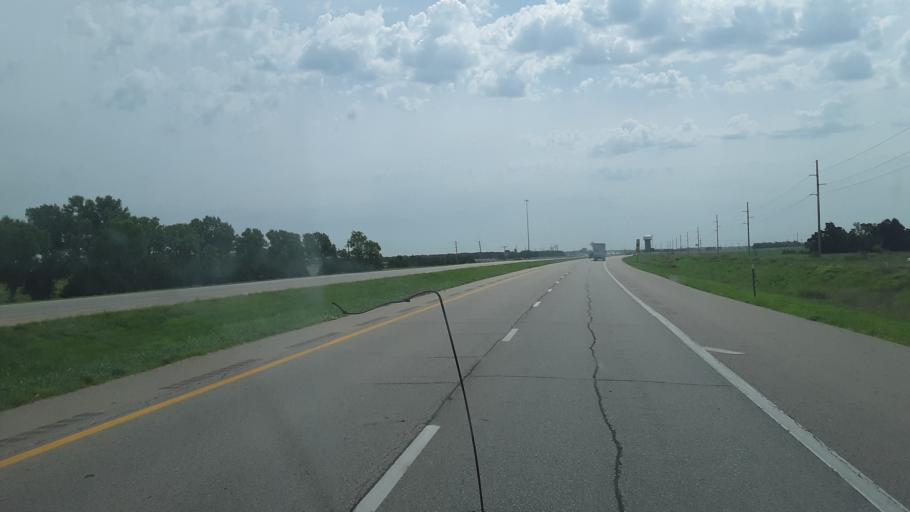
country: US
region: Kansas
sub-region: Reno County
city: South Hutchinson
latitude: 38.0142
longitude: -97.9650
